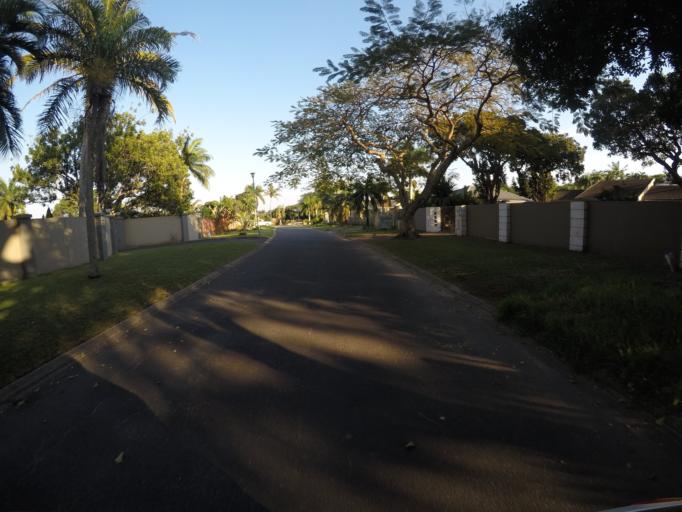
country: ZA
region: KwaZulu-Natal
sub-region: uThungulu District Municipality
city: Richards Bay
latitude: -28.7738
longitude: 32.1133
